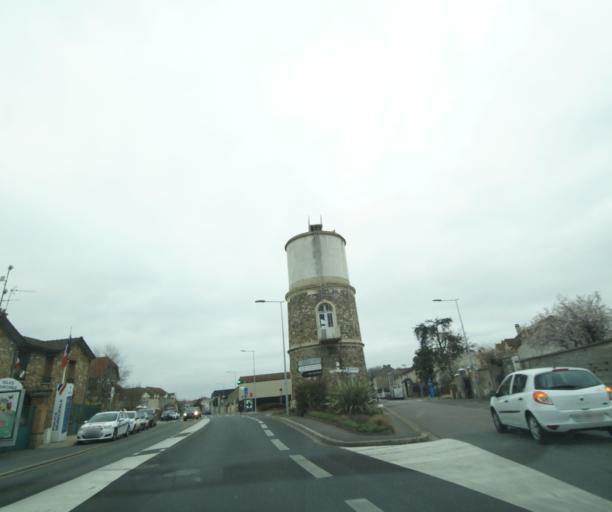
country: FR
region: Ile-de-France
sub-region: Departement des Yvelines
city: Carrieres-sous-Poissy
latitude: 48.9440
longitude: 2.0354
